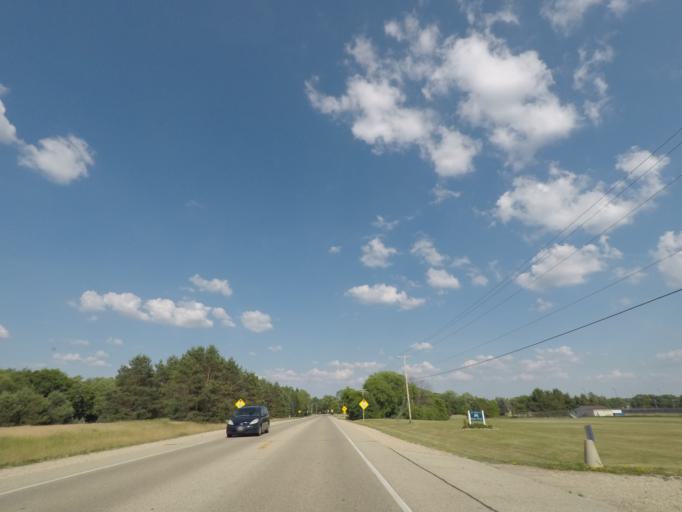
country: US
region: Wisconsin
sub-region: Walworth County
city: East Troy
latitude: 42.7916
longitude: -88.4188
